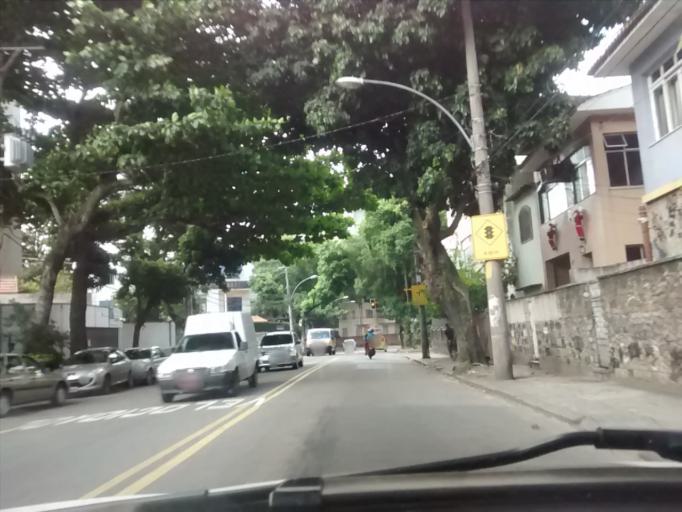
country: BR
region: Rio de Janeiro
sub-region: Rio De Janeiro
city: Rio de Janeiro
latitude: -22.9360
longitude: -43.2466
